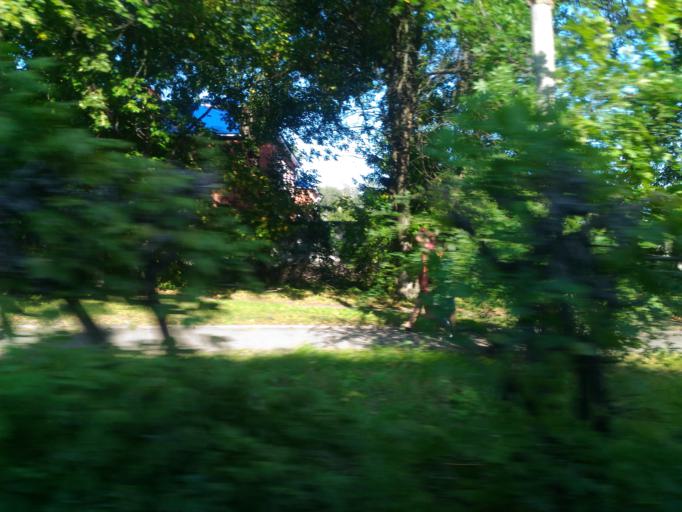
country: RU
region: Ulyanovsk
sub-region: Ulyanovskiy Rayon
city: Ulyanovsk
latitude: 54.3500
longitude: 48.5436
